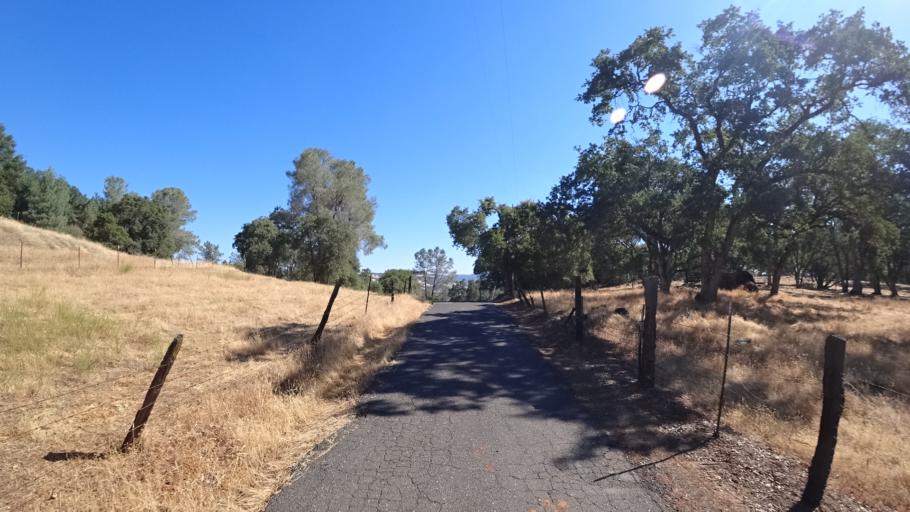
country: US
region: California
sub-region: Calaveras County
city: Angels Camp
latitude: 38.0813
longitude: -120.4818
